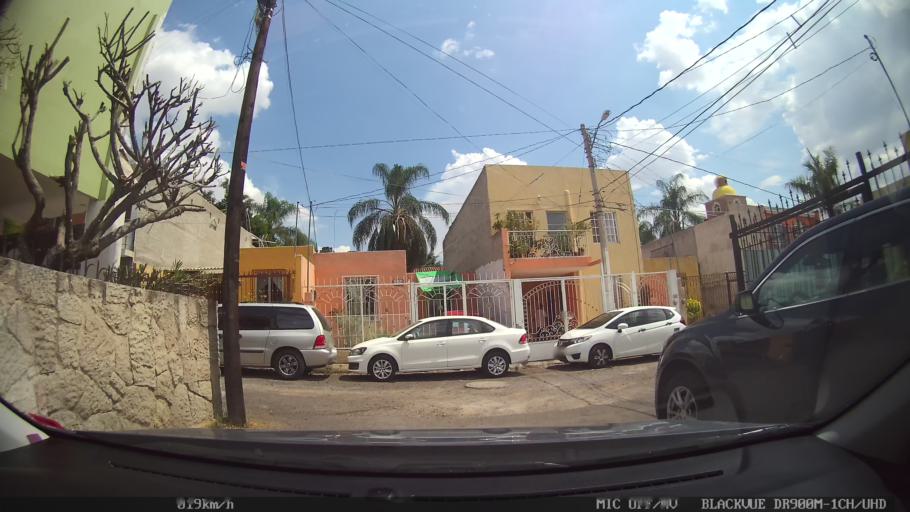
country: MX
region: Jalisco
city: Tonala
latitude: 20.6245
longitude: -103.2501
